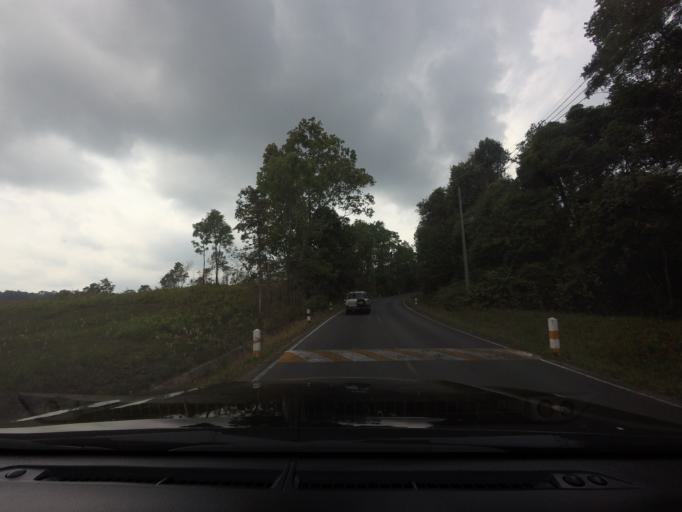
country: TH
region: Nakhon Nayok
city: Nakhon Nayok
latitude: 14.4234
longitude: 101.3707
